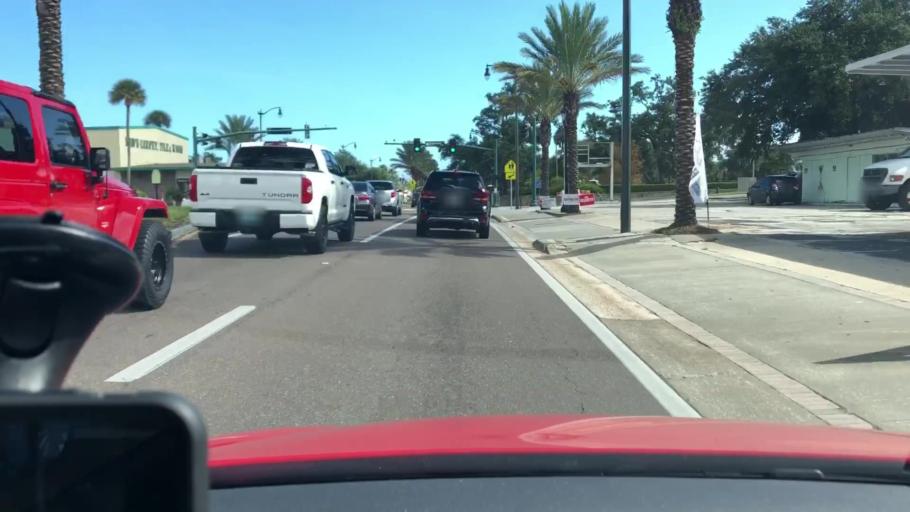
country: US
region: Florida
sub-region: Volusia County
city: Ormond Beach
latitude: 29.2841
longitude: -81.0593
